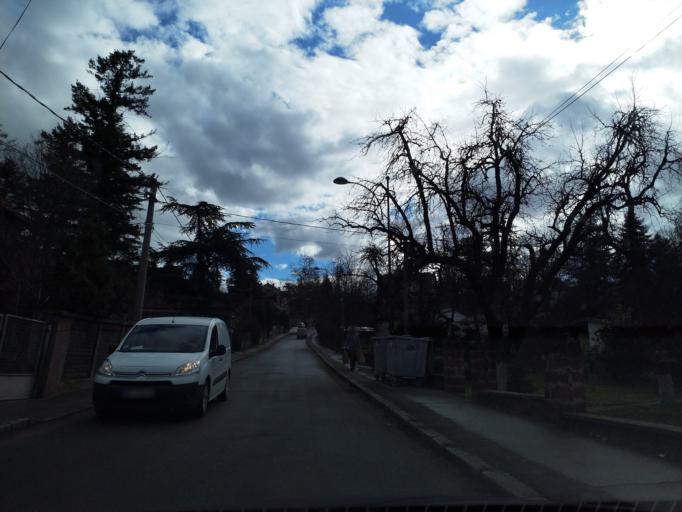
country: RS
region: Central Serbia
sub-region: Belgrade
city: Grocka
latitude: 44.6697
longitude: 20.7183
